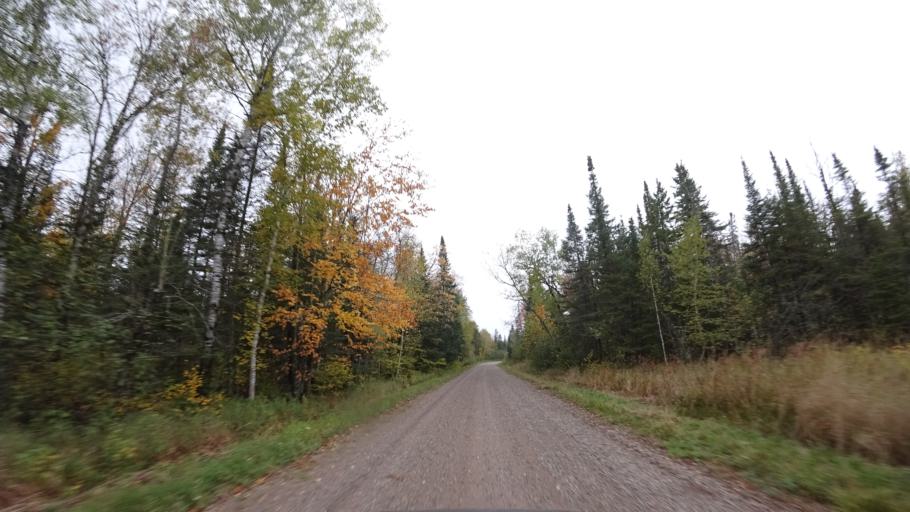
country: US
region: Wisconsin
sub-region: Sawyer County
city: Little Round Lake
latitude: 45.9742
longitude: -90.9884
